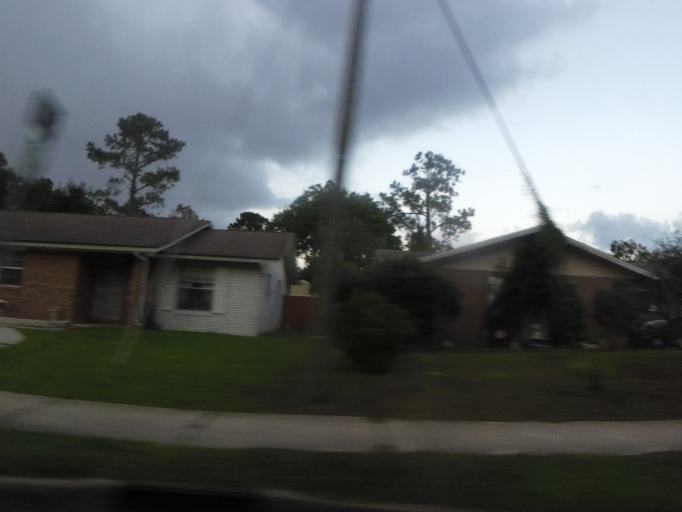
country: US
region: Florida
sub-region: Duval County
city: Jacksonville
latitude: 30.2392
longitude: -81.6076
